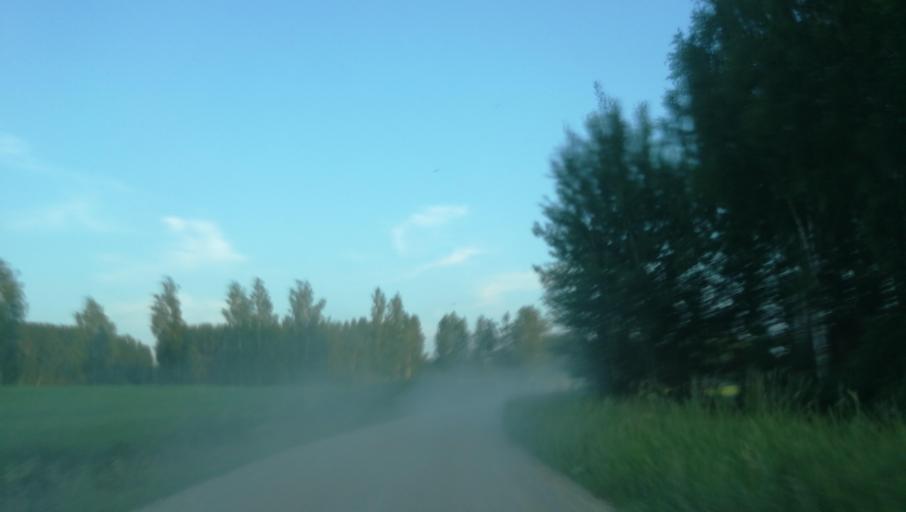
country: LV
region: Amatas Novads
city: Drabesi
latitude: 57.2595
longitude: 25.2220
